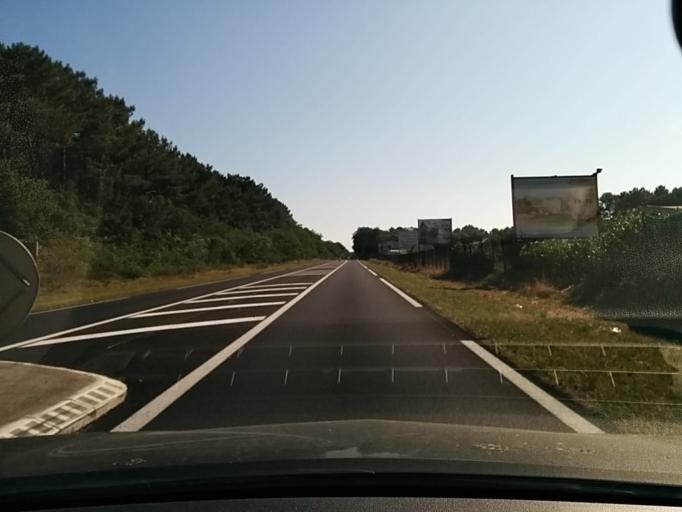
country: FR
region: Aquitaine
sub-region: Departement des Landes
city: Labenne
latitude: 43.6114
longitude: -1.4048
